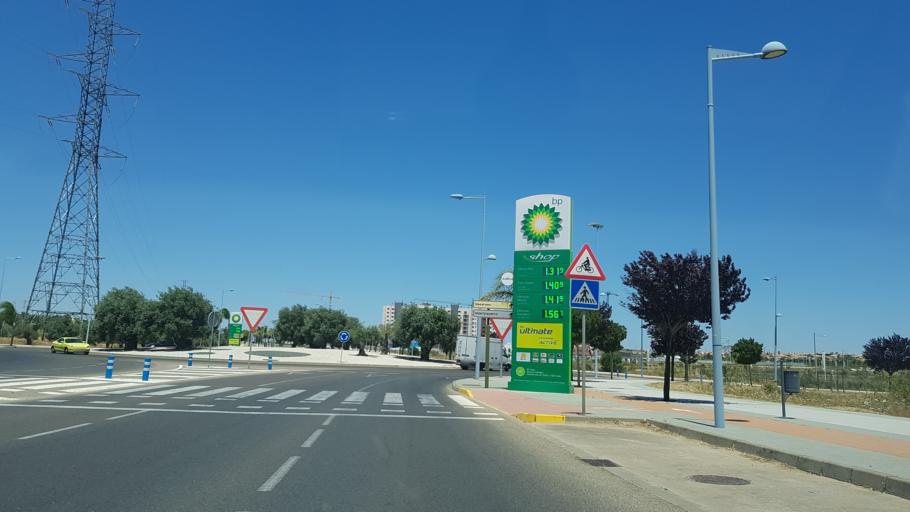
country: ES
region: Andalusia
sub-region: Provincia de Sevilla
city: Dos Hermanas
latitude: 37.3145
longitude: -5.9409
